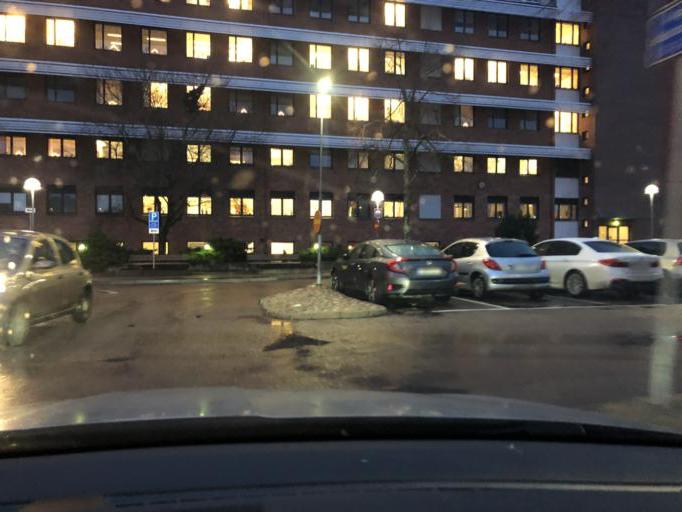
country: SE
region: Vaermland
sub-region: Karlstads Kommun
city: Karlstad
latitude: 59.3743
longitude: 13.4801
